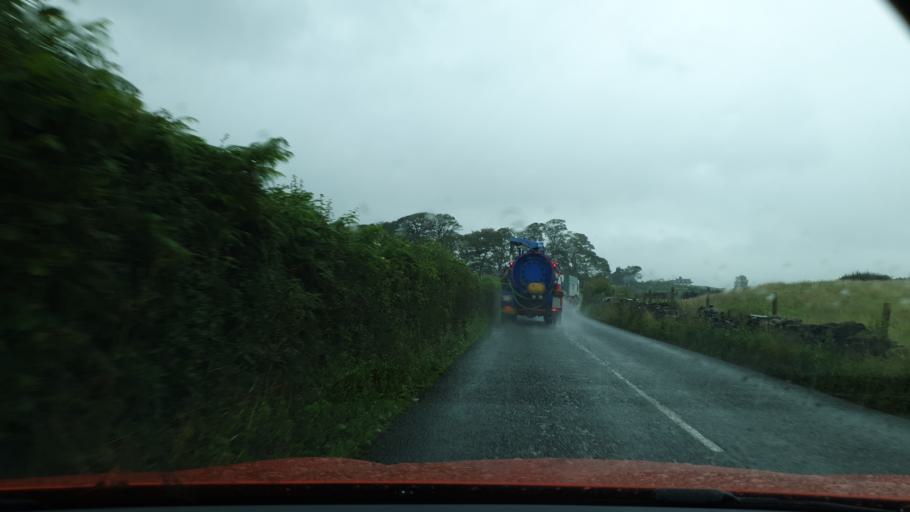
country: GB
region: England
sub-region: Cumbria
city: Millom
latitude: 54.2744
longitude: -3.2220
